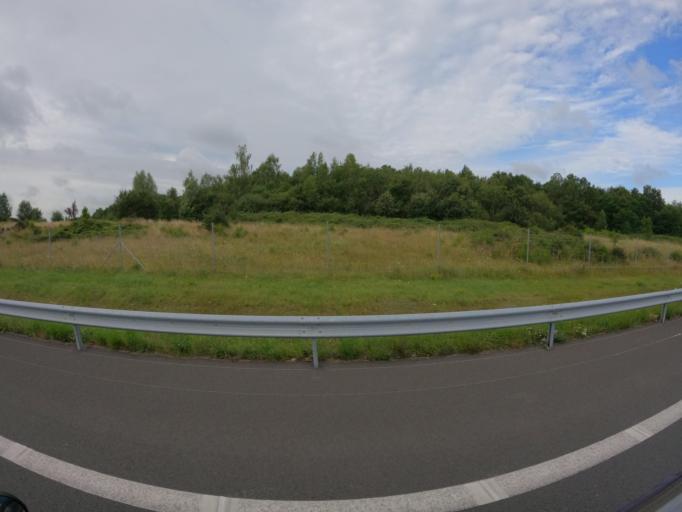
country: FR
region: Centre
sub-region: Departement d'Indre-et-Loire
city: Langeais
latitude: 47.3404
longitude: 0.4250
